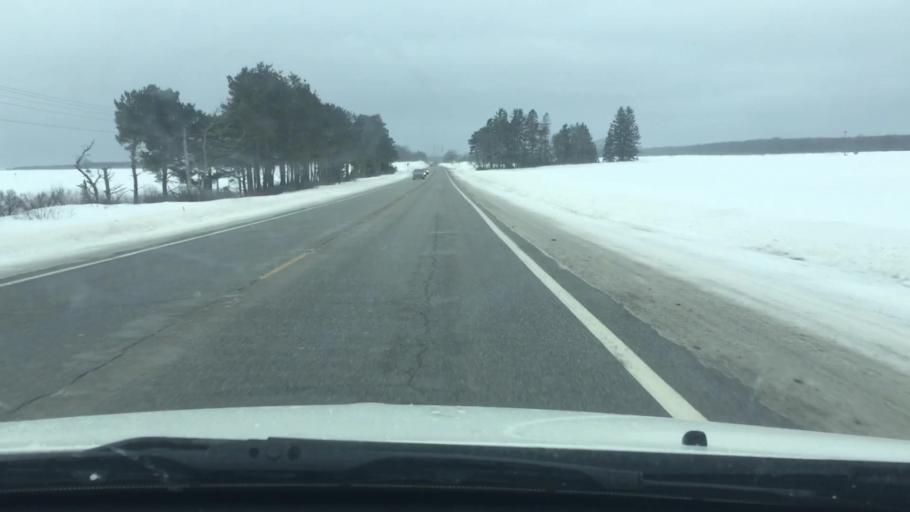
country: US
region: Michigan
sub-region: Otsego County
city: Gaylord
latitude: 45.0664
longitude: -84.8733
